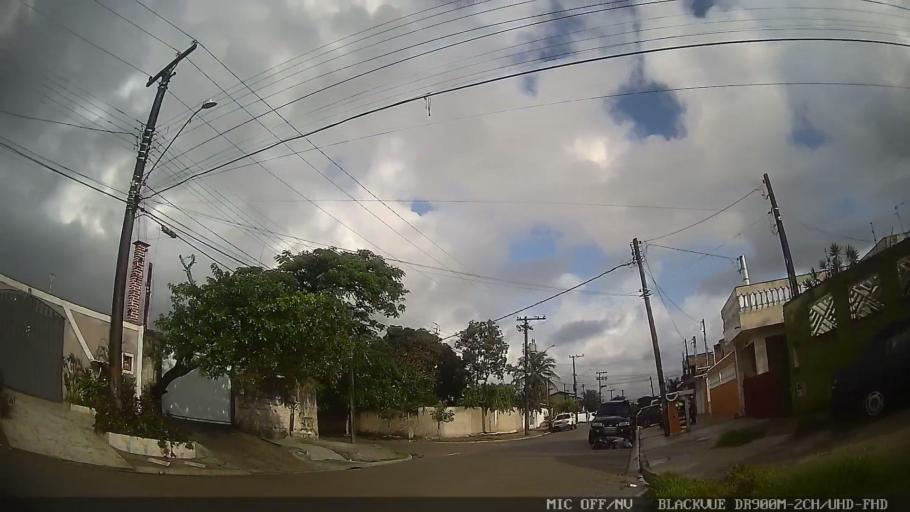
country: BR
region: Sao Paulo
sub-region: Itanhaem
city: Itanhaem
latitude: -24.1834
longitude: -46.8569
